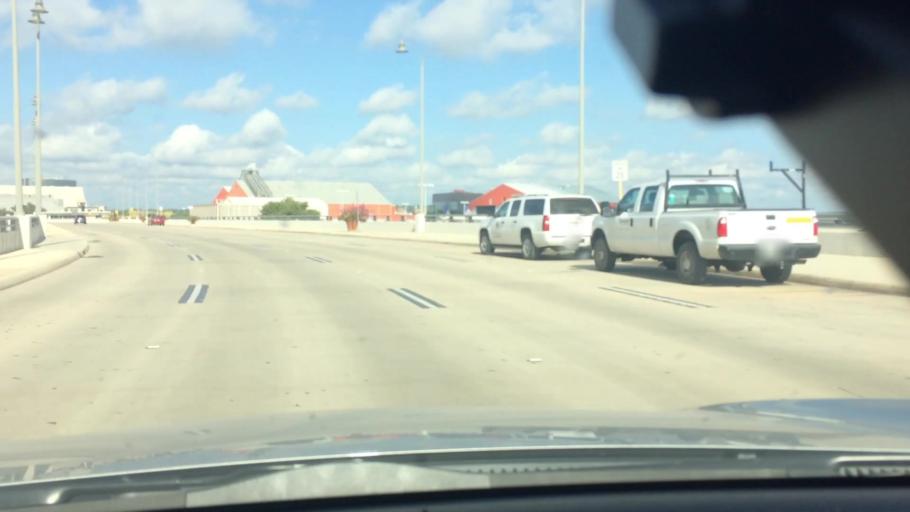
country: US
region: Texas
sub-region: Bexar County
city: Castle Hills
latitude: 29.5281
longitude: -98.4740
